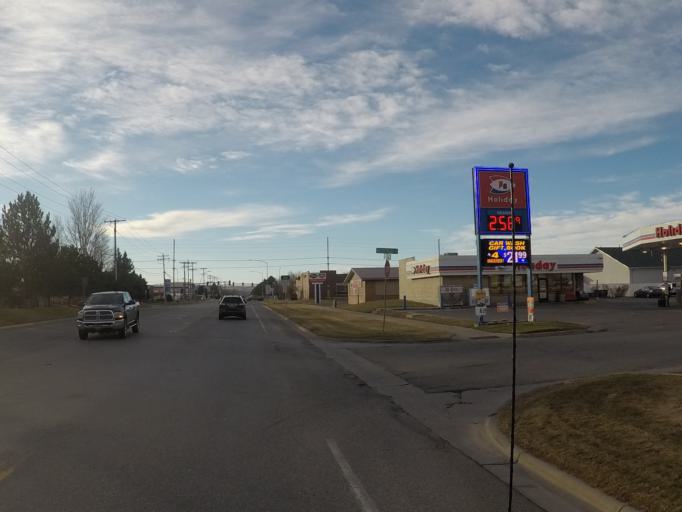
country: US
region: Montana
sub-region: Yellowstone County
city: Billings
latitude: 45.7571
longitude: -108.5969
